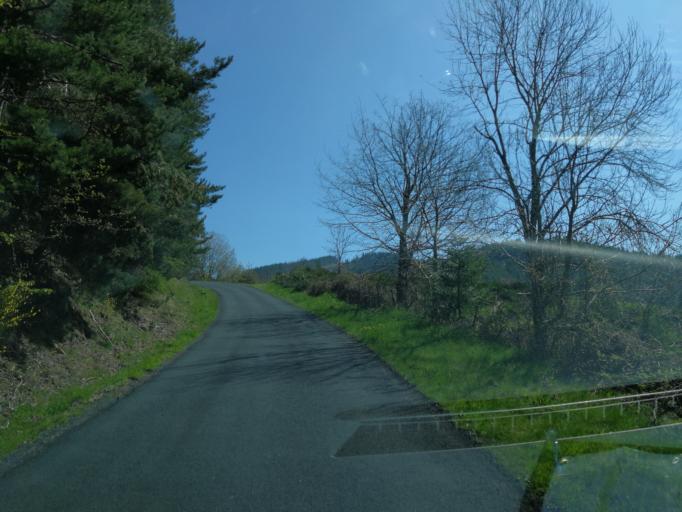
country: FR
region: Rhone-Alpes
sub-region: Departement de l'Ardeche
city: Le Cheylard
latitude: 44.9381
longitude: 4.4253
